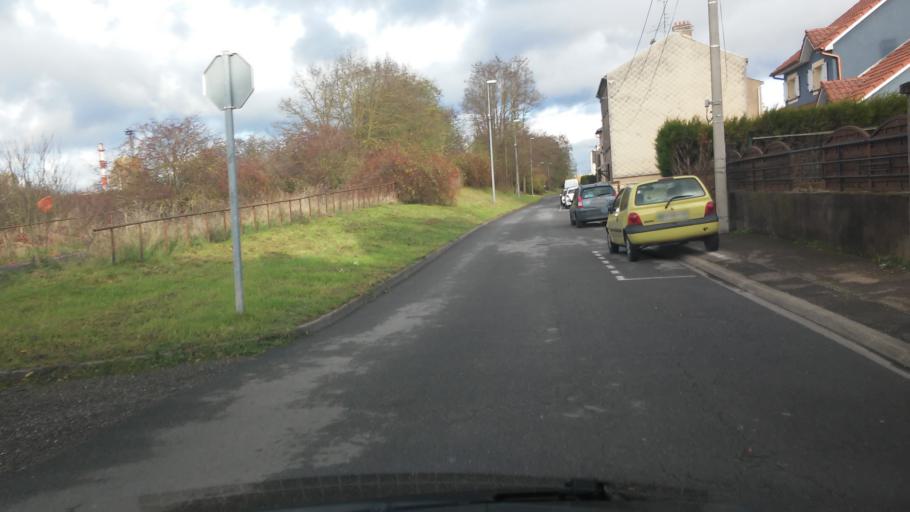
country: FR
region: Lorraine
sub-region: Departement de la Moselle
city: Talange
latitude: 49.2364
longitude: 6.1629
